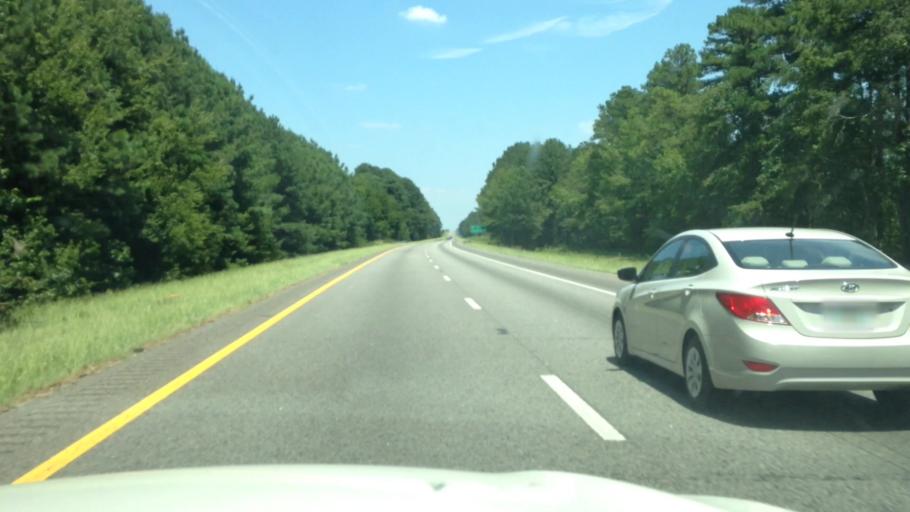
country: US
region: South Carolina
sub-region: Dillon County
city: Dillon
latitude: 34.4267
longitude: -79.4028
